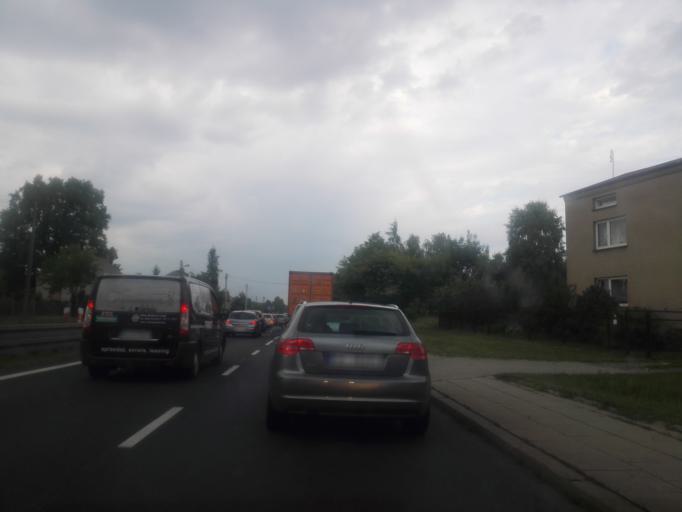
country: PL
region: Silesian Voivodeship
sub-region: Powiat czestochowski
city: Kamienica Polska
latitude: 50.6978
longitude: 19.1398
